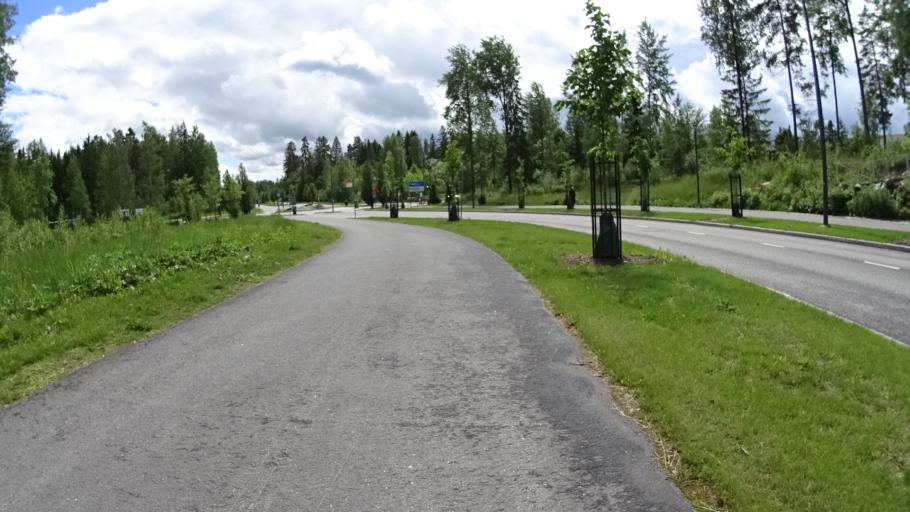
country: FI
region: Uusimaa
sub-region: Helsinki
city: Kilo
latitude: 60.2388
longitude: 24.8212
